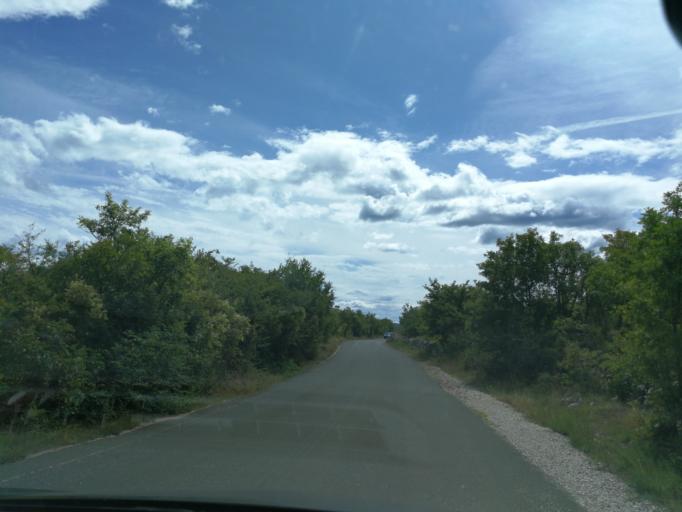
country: HR
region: Primorsko-Goranska
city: Omisalj
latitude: 45.1893
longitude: 14.5854
